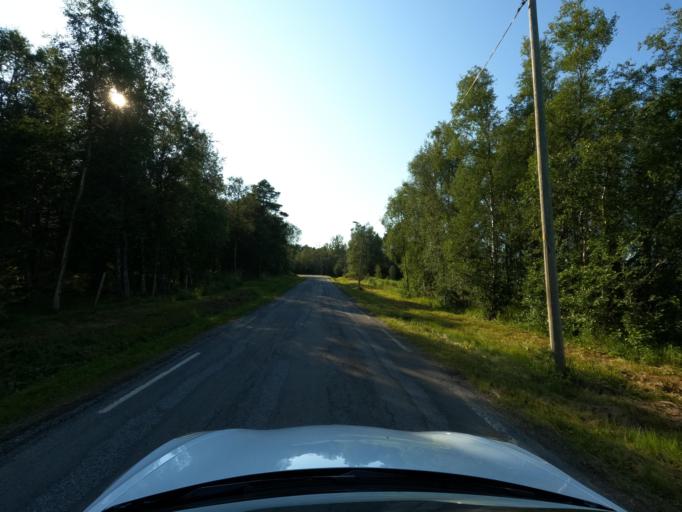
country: NO
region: Nordland
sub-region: Narvik
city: Bjerkvik
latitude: 68.4821
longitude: 17.5309
